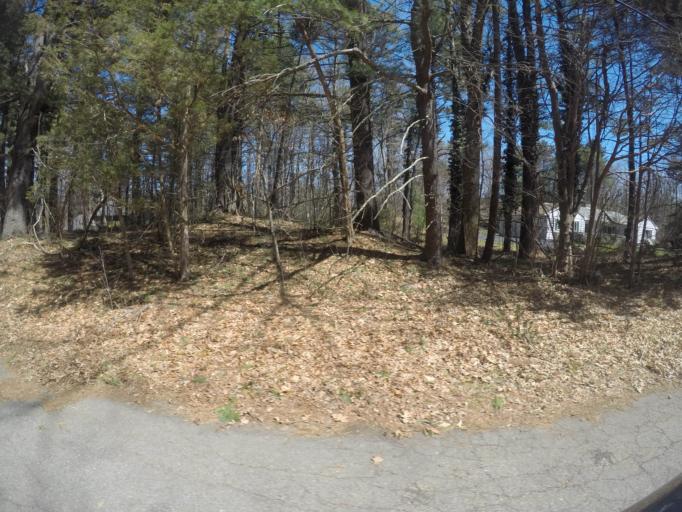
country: US
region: Massachusetts
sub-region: Bristol County
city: Easton
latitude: 42.0455
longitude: -71.0905
